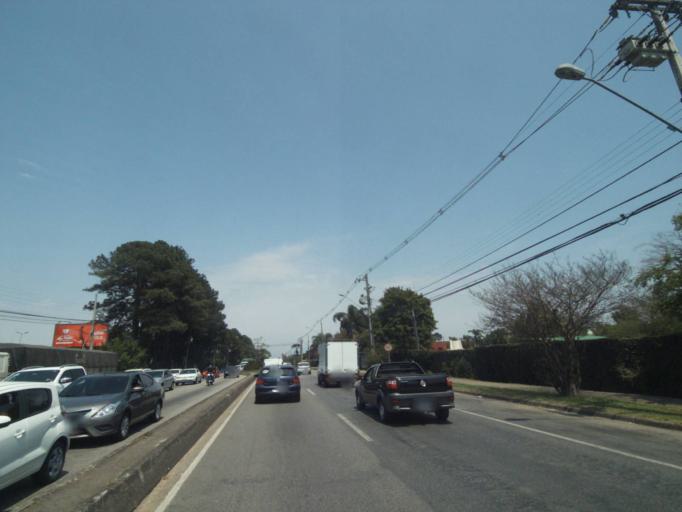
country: BR
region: Parana
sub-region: Curitiba
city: Curitiba
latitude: -25.4871
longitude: -49.3194
